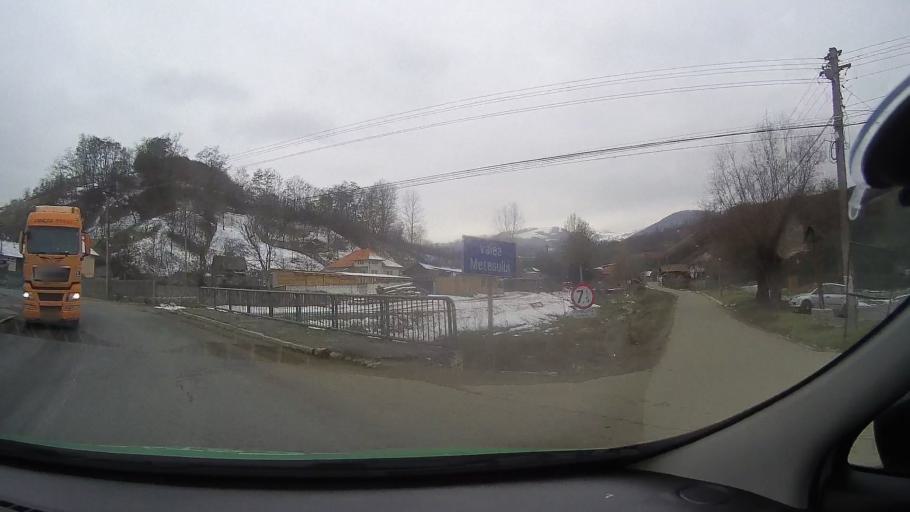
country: RO
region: Alba
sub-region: Comuna Metes
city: Metes
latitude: 46.0939
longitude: 23.4191
